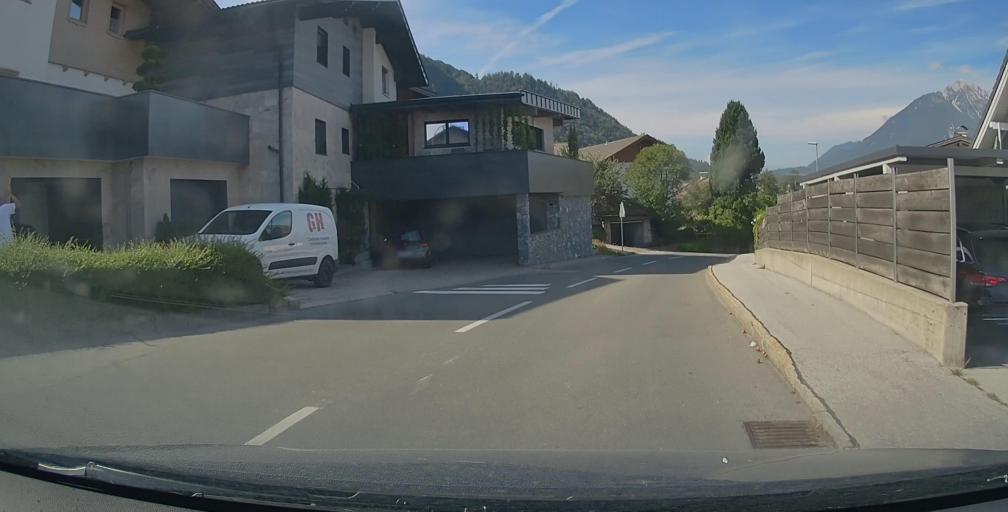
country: AT
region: Tyrol
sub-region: Politischer Bezirk Schwaz
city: Jenbach
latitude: 47.3837
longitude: 11.7839
